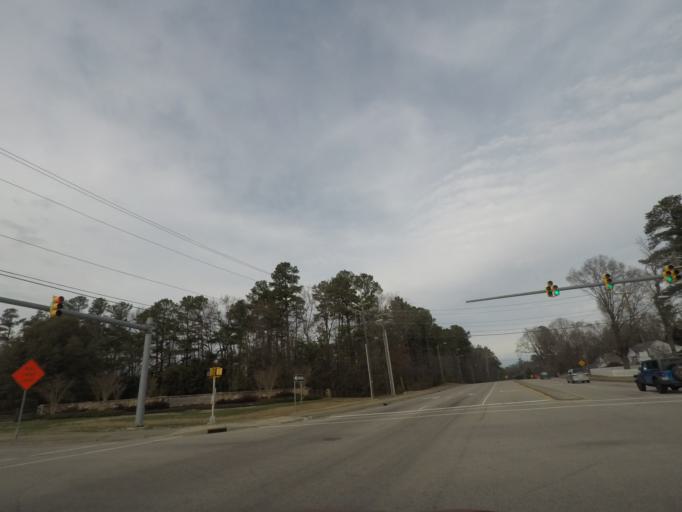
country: US
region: North Carolina
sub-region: Durham County
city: Durham
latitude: 36.0375
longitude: -78.9356
